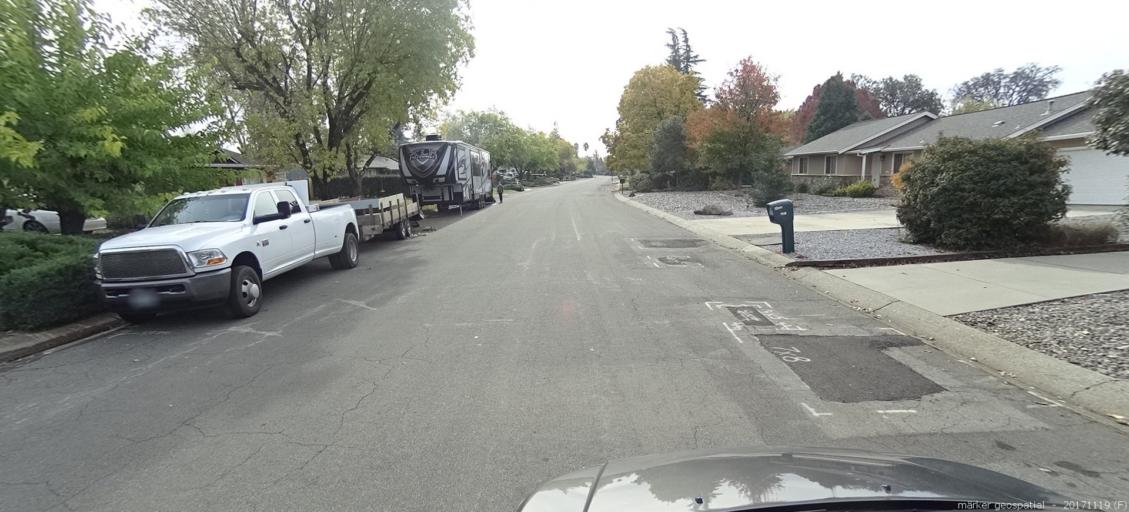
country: US
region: California
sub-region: Shasta County
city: Anderson
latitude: 40.4930
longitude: -122.3083
